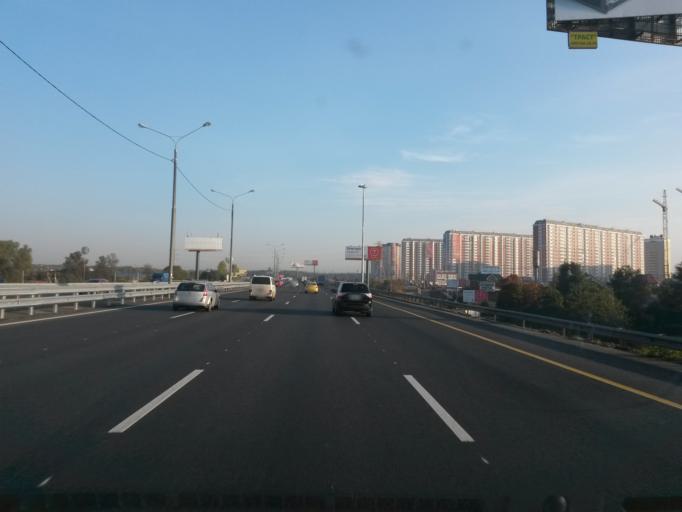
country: RU
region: Moscow
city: Annino
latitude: 55.5269
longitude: 37.6104
